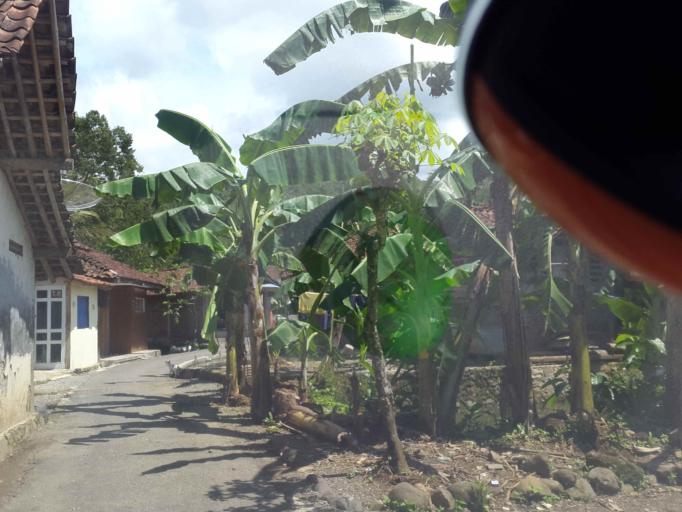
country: ID
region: Central Java
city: Wonosobo
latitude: -7.3527
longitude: 109.6701
